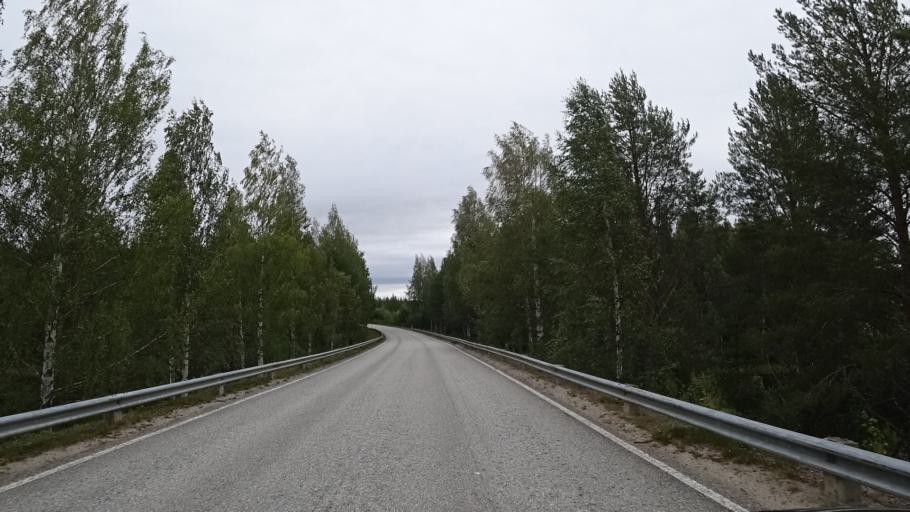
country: FI
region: North Karelia
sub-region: Pielisen Karjala
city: Lieksa
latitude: 63.3474
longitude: 30.2647
